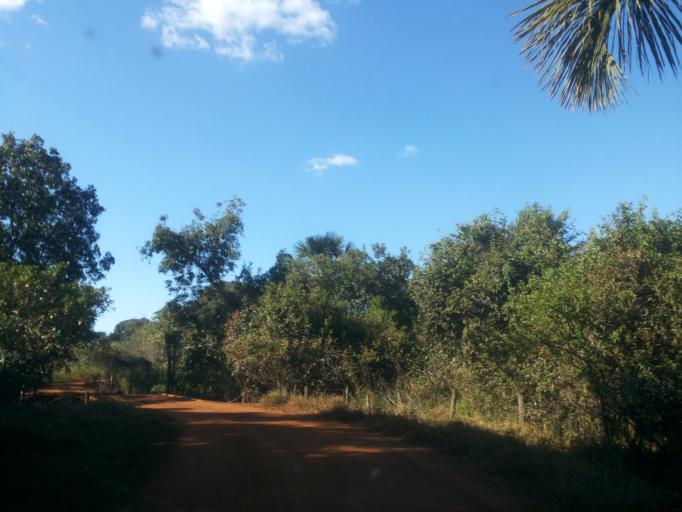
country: BR
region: Minas Gerais
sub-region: Centralina
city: Centralina
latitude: -18.7396
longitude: -49.1599
